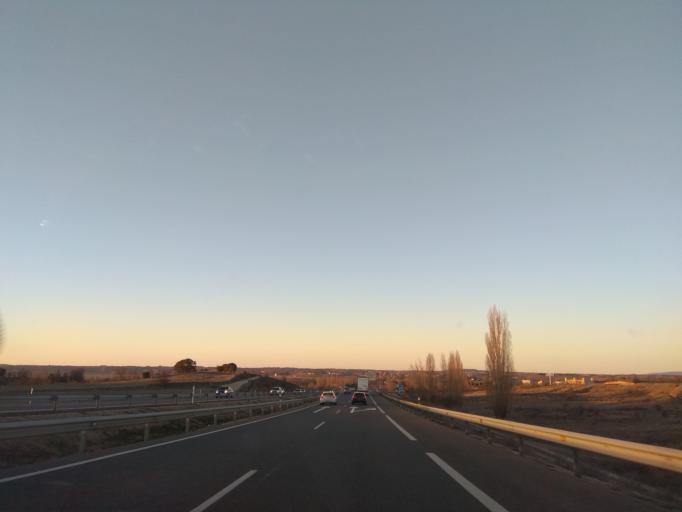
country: ES
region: Castille and Leon
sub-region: Provincia de Burgos
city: Quintana del Pidio
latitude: 41.7467
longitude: -3.6894
